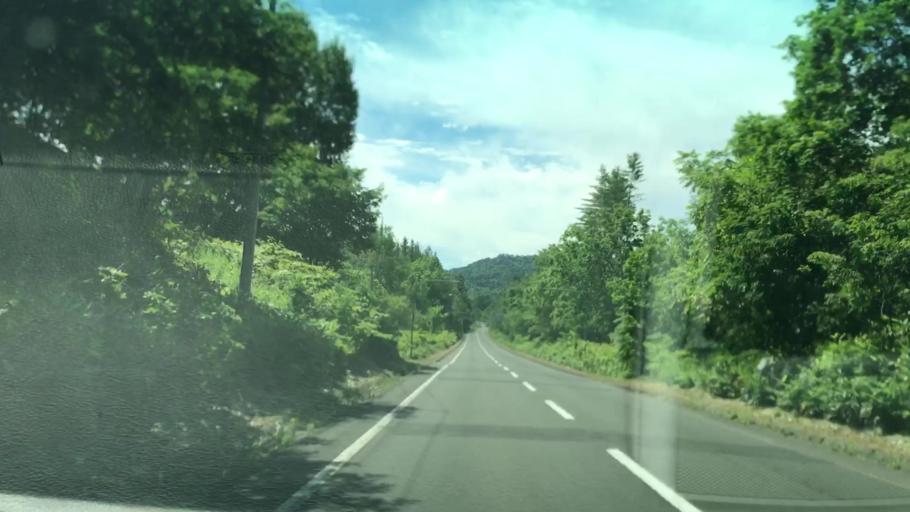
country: JP
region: Hokkaido
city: Shimo-furano
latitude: 42.9646
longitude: 142.4278
